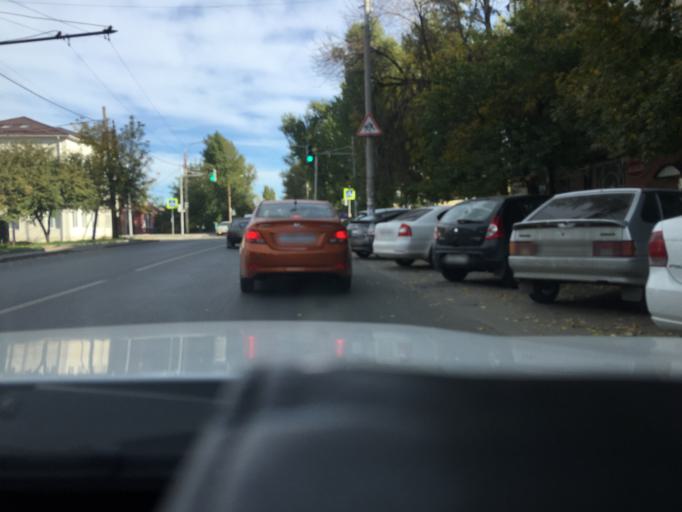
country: RU
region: Rostov
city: Imeni Chkalova
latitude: 47.2686
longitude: 39.7883
